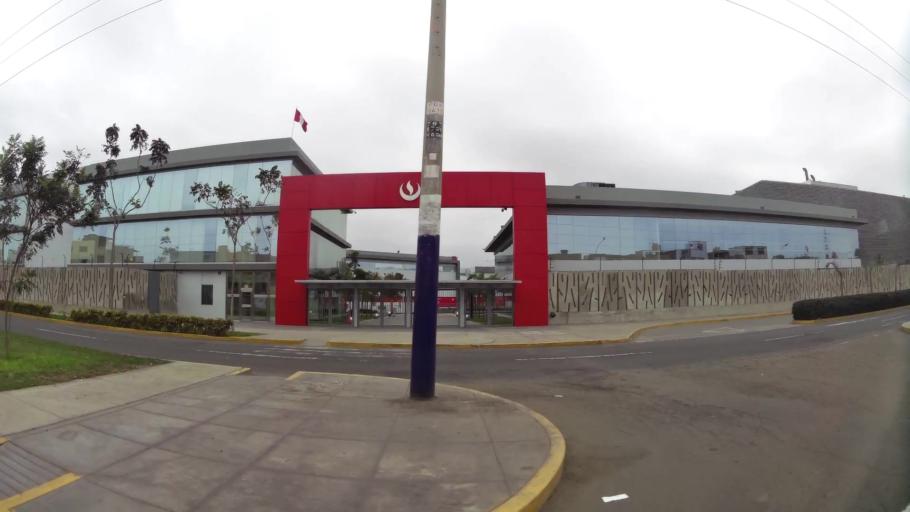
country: PE
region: Lima
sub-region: Lima
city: Surco
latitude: -12.1987
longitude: -77.0085
